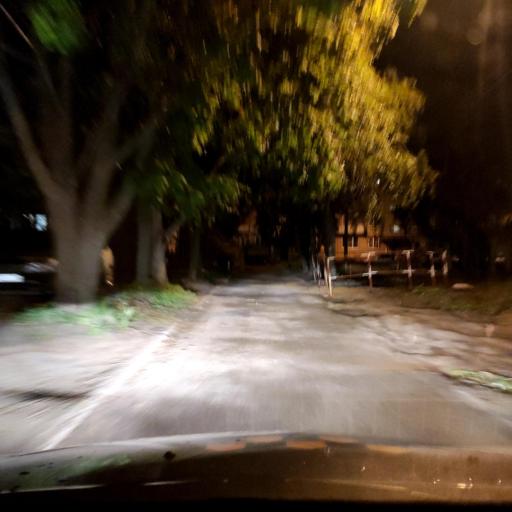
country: RU
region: Voronezj
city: Maslovka
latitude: 51.5879
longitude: 39.3213
